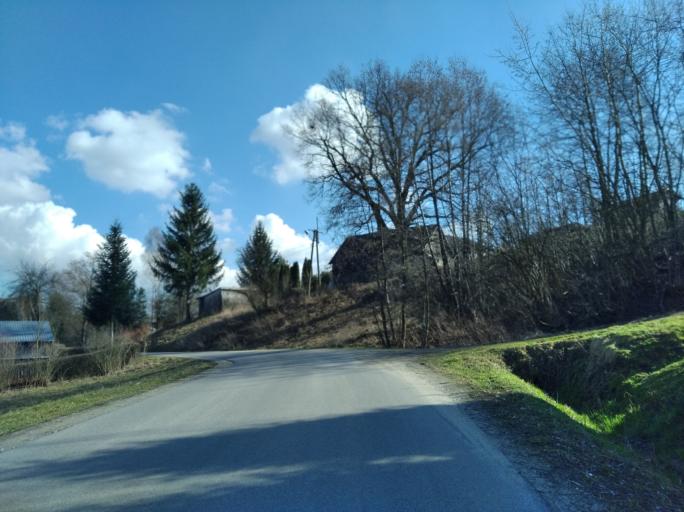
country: PL
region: Subcarpathian Voivodeship
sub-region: Powiat strzyzowski
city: Wisniowa
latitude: 49.8575
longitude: 21.6530
